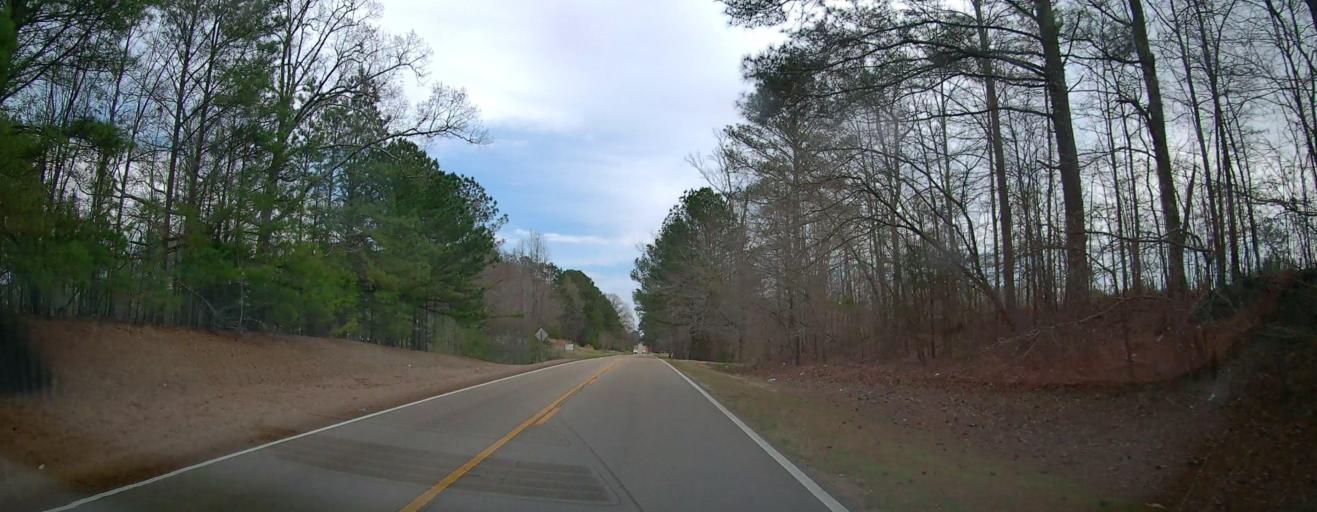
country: US
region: Mississippi
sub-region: Itawamba County
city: Mantachie
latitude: 34.2572
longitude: -88.5027
